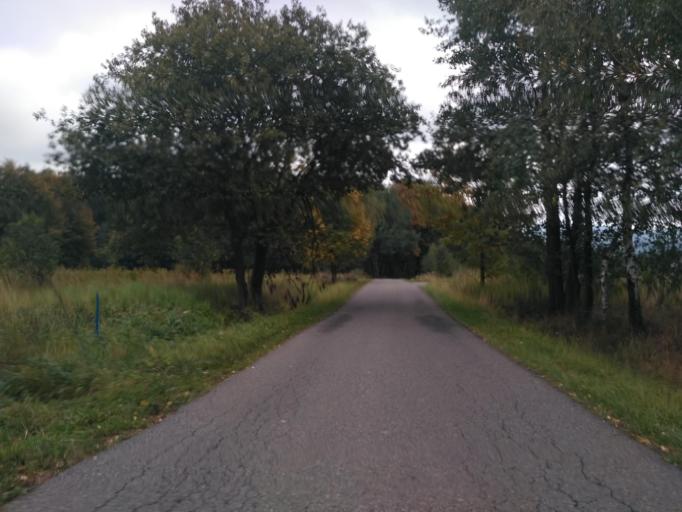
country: PL
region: Subcarpathian Voivodeship
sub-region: Powiat ropczycko-sedziszowski
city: Niedzwiada
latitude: 49.9538
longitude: 21.4573
